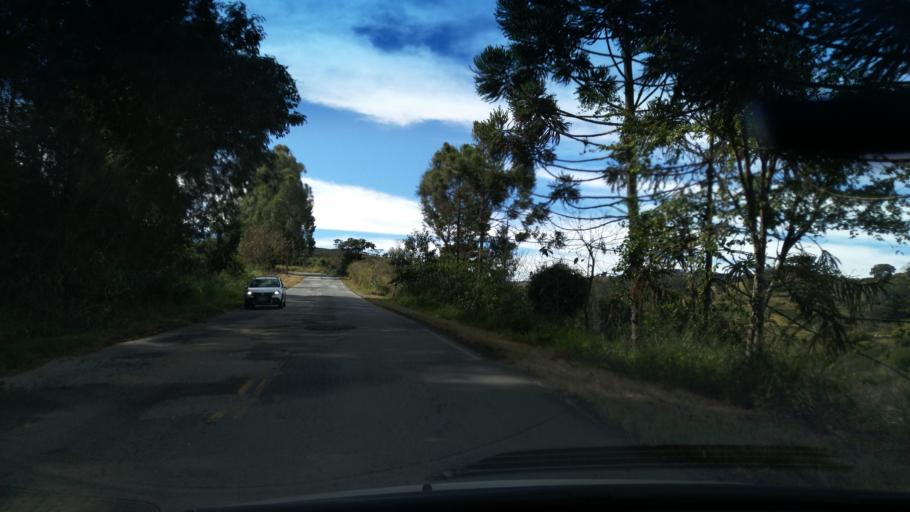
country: BR
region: Minas Gerais
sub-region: Andradas
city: Andradas
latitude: -22.0617
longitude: -46.3764
